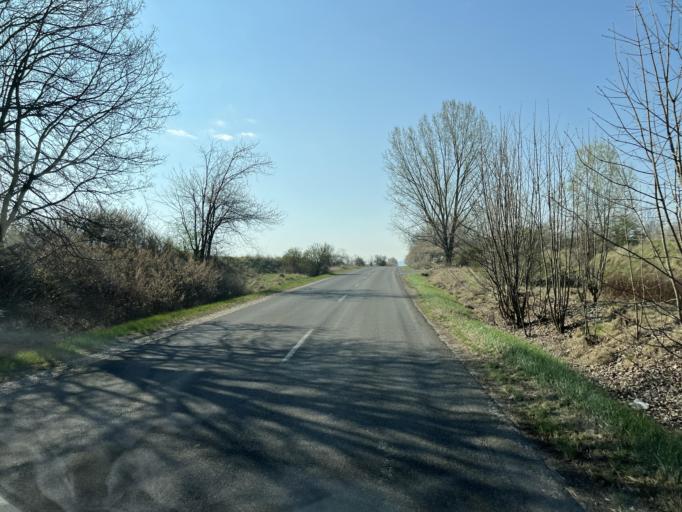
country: HU
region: Pest
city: Galgamacsa
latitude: 47.6944
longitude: 19.4019
